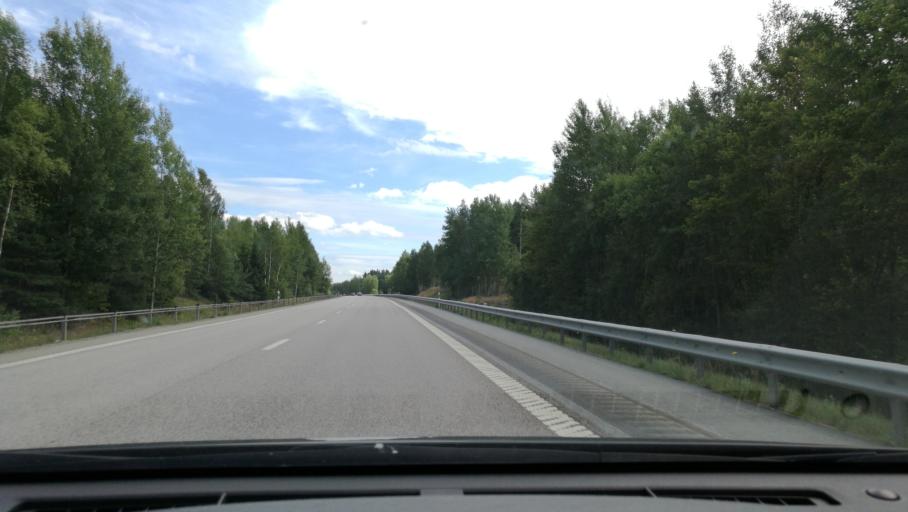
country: SE
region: Stockholm
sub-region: Upplands-Bro Kommun
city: Bro
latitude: 59.5466
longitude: 17.5993
